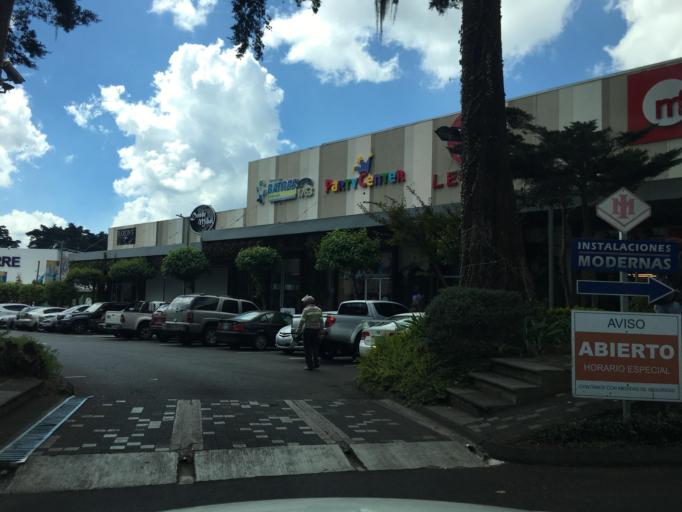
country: GT
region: Guatemala
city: Santa Catarina Pinula
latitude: 14.5586
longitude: -90.4628
